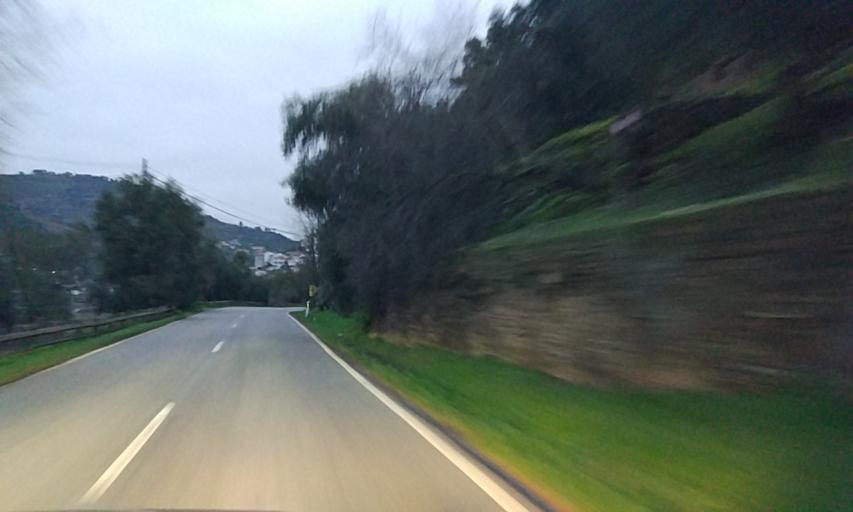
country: PT
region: Vila Real
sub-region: Sabrosa
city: Vilela
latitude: 41.1834
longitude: -7.5481
